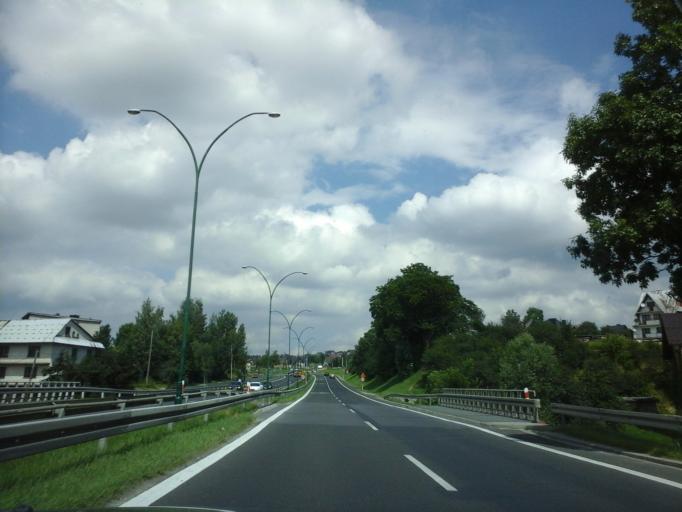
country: PL
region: Lesser Poland Voivodeship
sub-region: Powiat nowotarski
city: Nowy Targ
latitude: 49.4867
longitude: 20.0190
